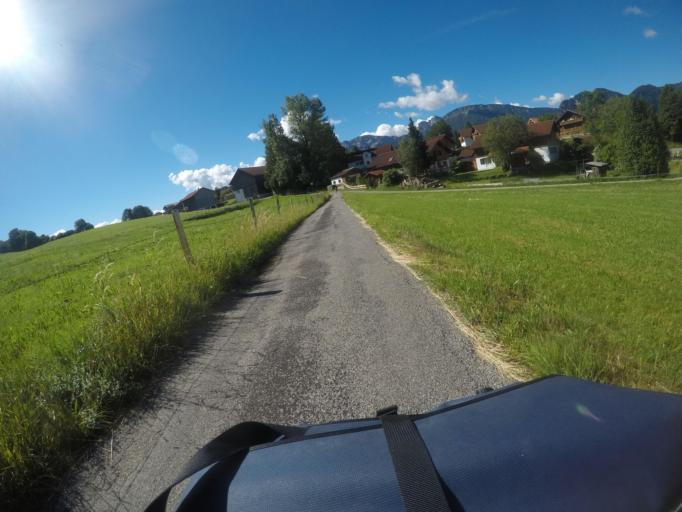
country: DE
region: Bavaria
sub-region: Swabia
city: Pfronten
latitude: 47.5985
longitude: 10.5670
